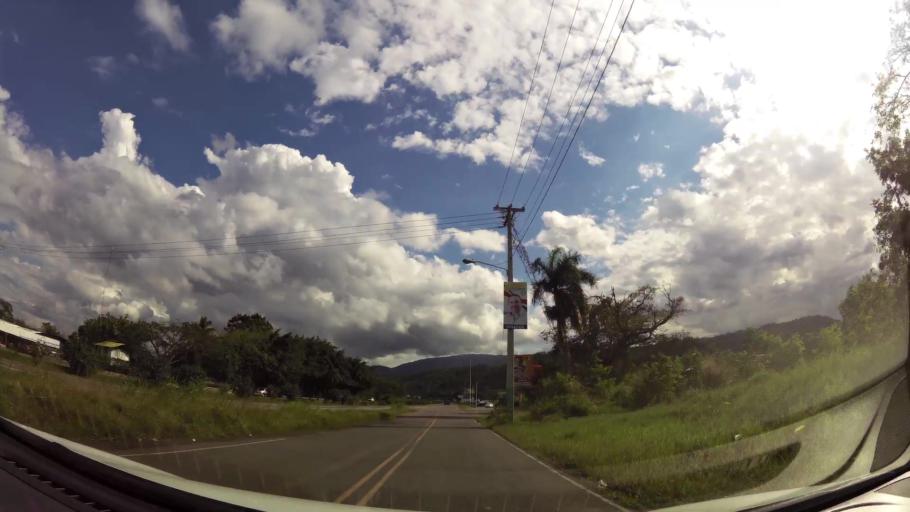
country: DO
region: La Vega
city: Concepcion de La Vega
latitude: 19.1948
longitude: -70.4983
